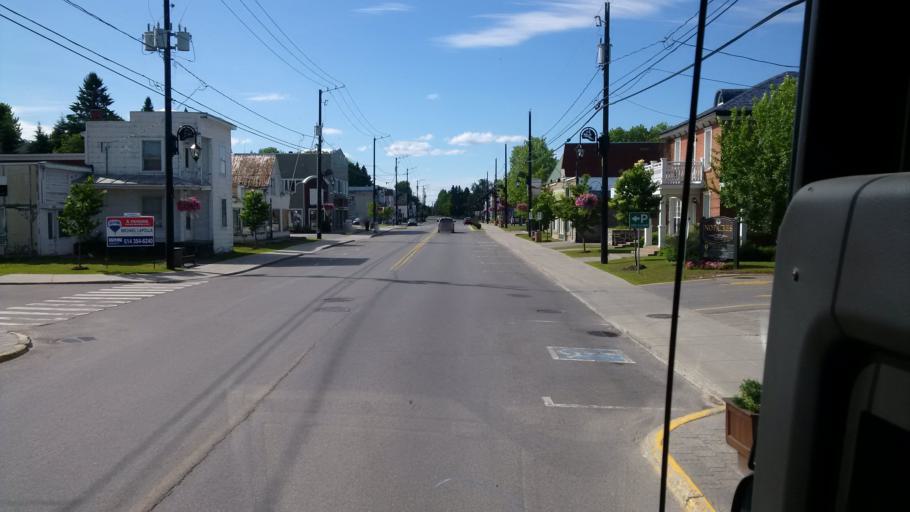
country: CA
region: Quebec
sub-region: Laurentides
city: Riviere-Rouge
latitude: 46.4141
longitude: -74.8711
